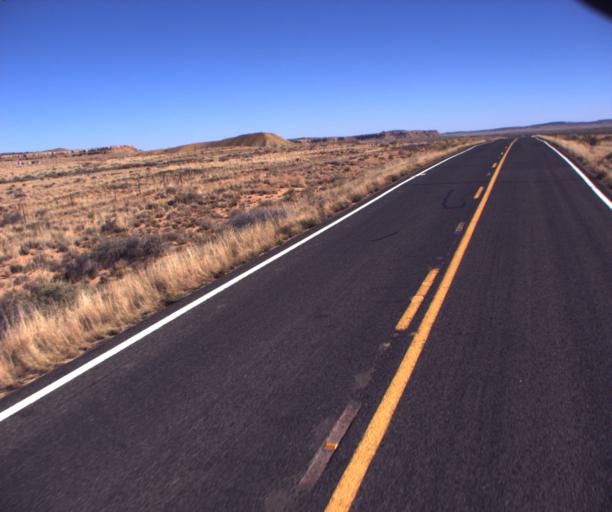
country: US
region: Arizona
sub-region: Navajo County
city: First Mesa
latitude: 35.9758
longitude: -110.7608
